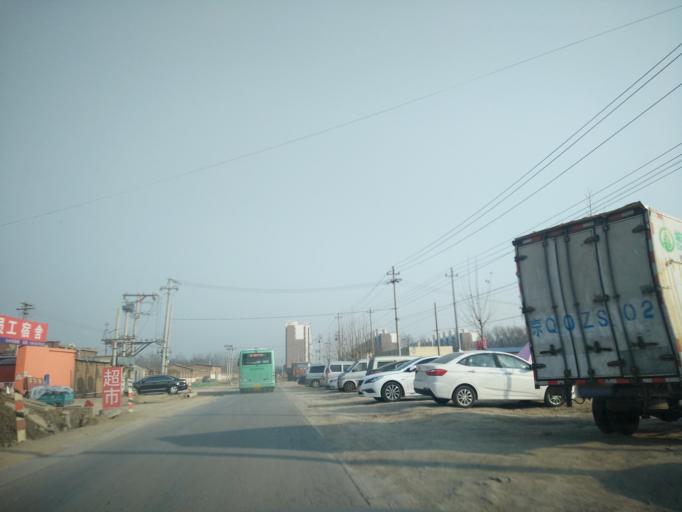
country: CN
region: Beijing
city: Xingfeng
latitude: 39.7171
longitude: 116.3875
